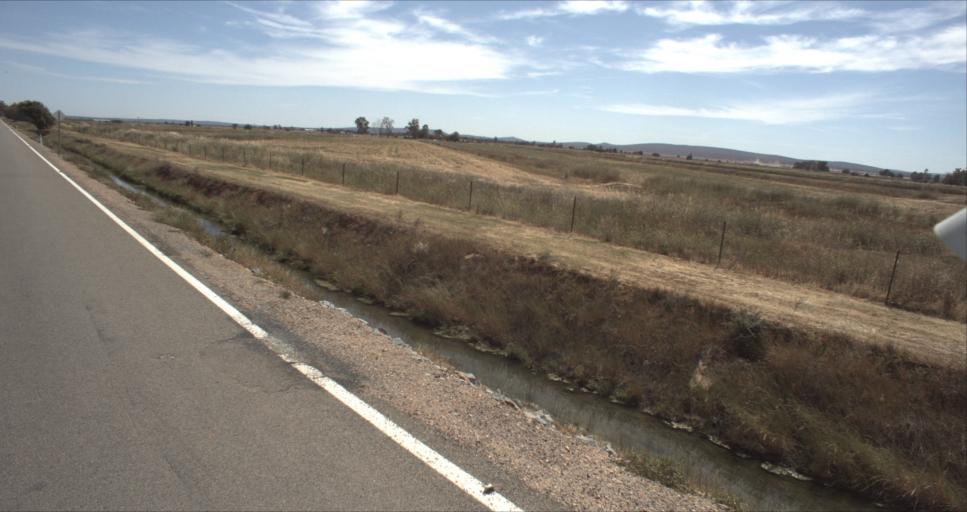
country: AU
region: New South Wales
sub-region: Leeton
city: Leeton
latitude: -34.5591
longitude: 146.4412
